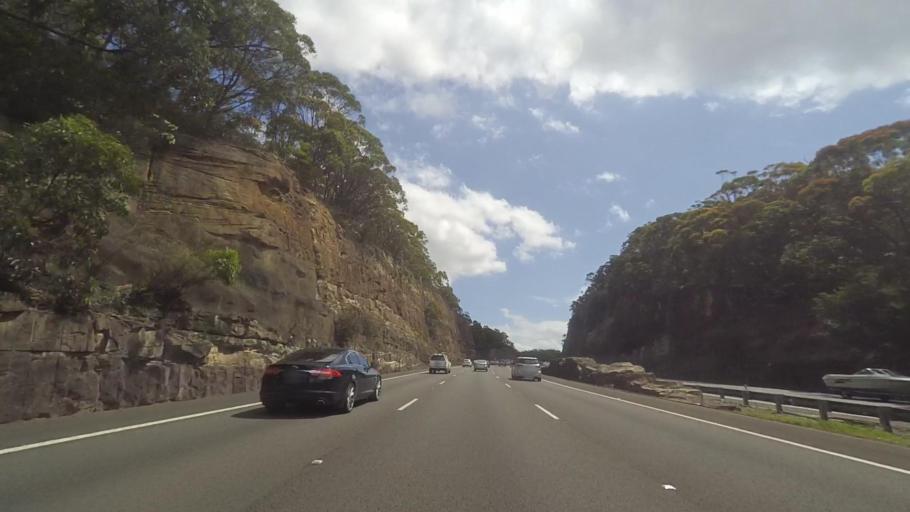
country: AU
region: New South Wales
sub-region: Hornsby Shire
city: Berowra
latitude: -33.5820
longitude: 151.1895
